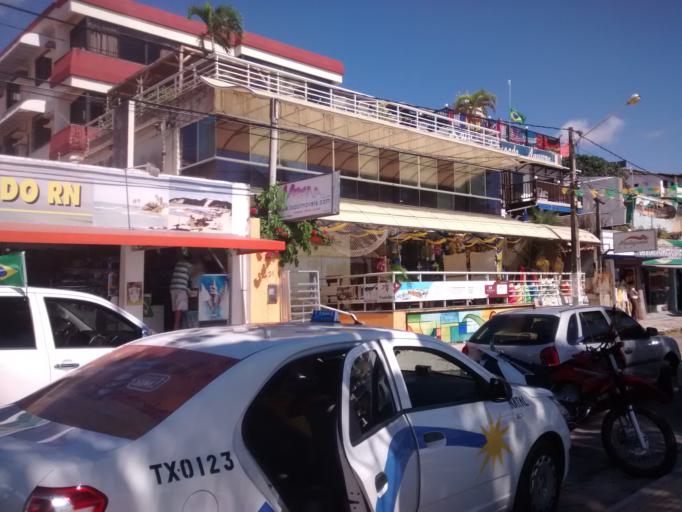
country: BR
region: Rio Grande do Norte
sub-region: Natal
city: Natal
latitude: -5.8821
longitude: -35.1706
